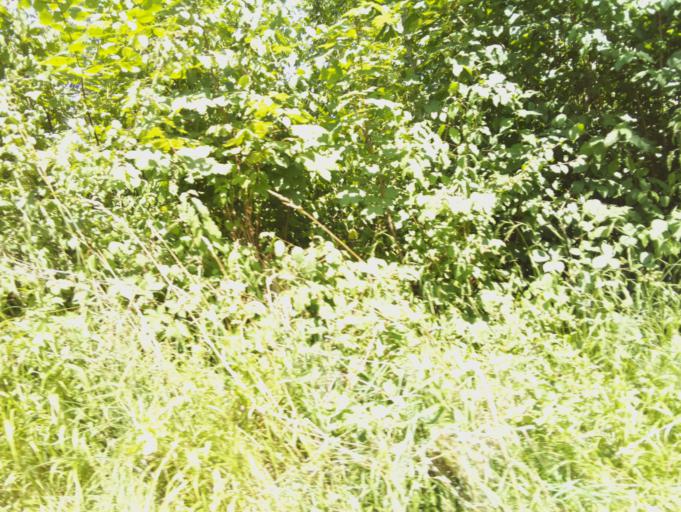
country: CH
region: Zurich
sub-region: Bezirk Andelfingen
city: Kleinandelfingen
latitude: 47.6209
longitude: 8.6925
